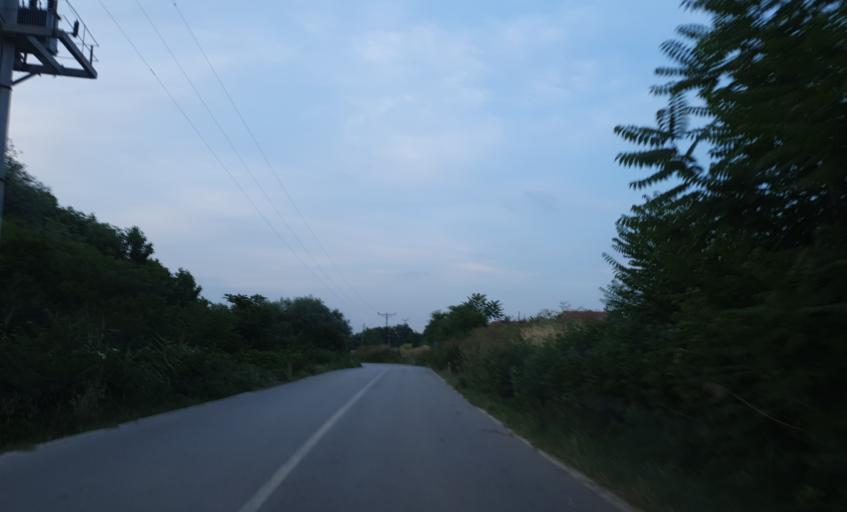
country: TR
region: Tekirdag
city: Beyazkoy
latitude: 41.3788
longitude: 27.6142
